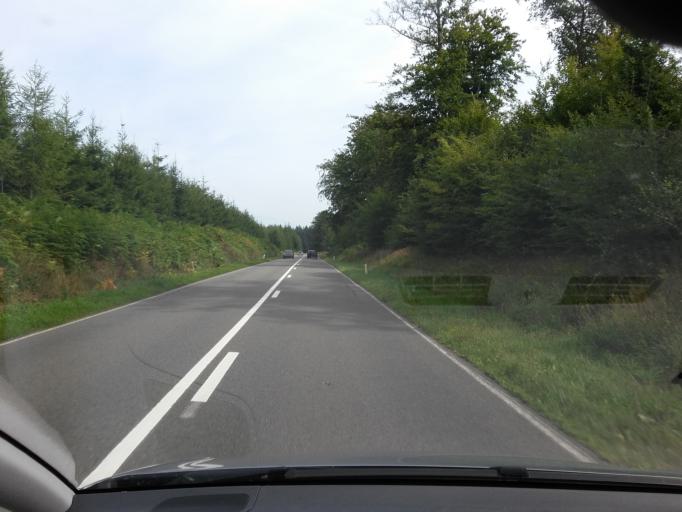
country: BE
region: Wallonia
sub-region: Province du Luxembourg
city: Chiny
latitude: 49.7679
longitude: 5.3227
